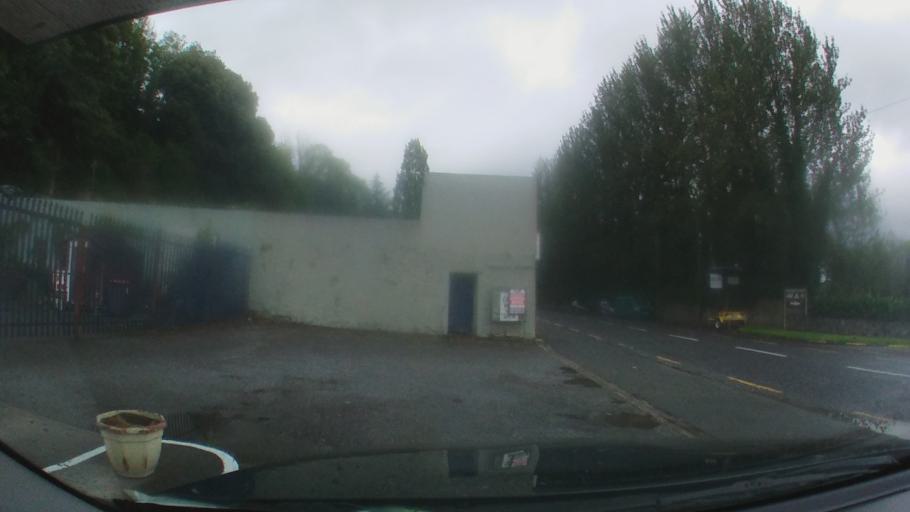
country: IE
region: Munster
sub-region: County Cork
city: Fermoy
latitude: 52.1399
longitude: -8.1101
